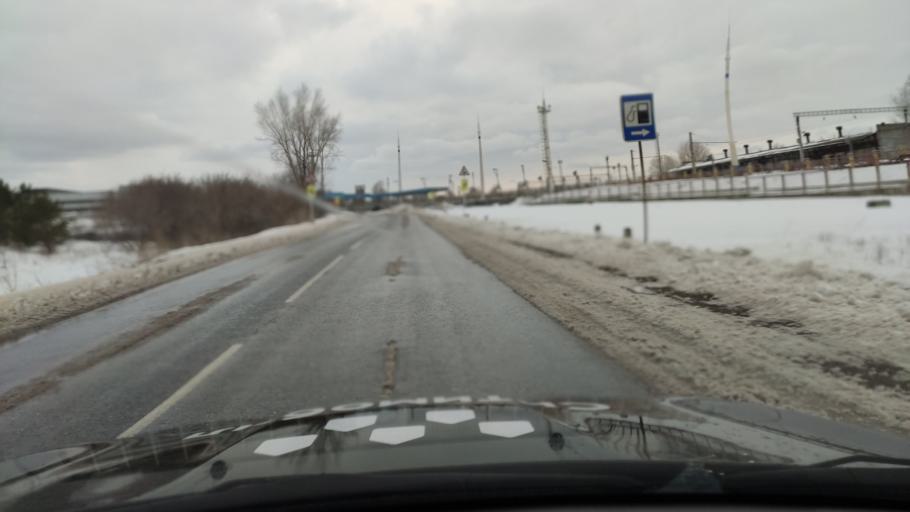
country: RU
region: Samara
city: Povolzhskiy
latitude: 53.5518
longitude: 49.6192
